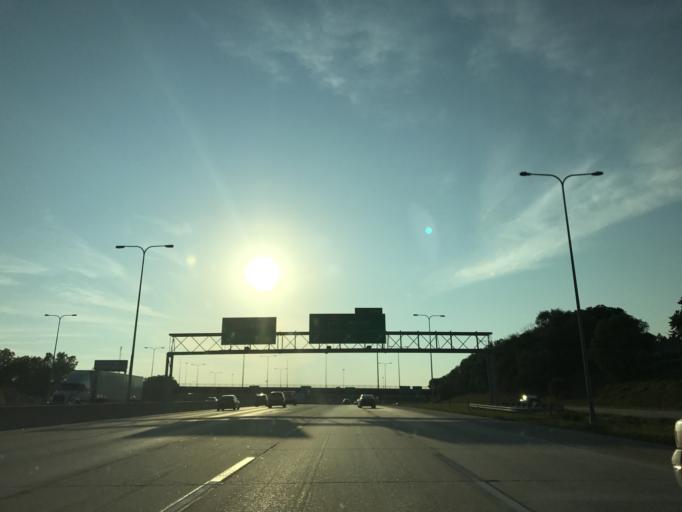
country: US
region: Nebraska
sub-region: Douglas County
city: Ralston
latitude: 41.2234
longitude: -96.0781
